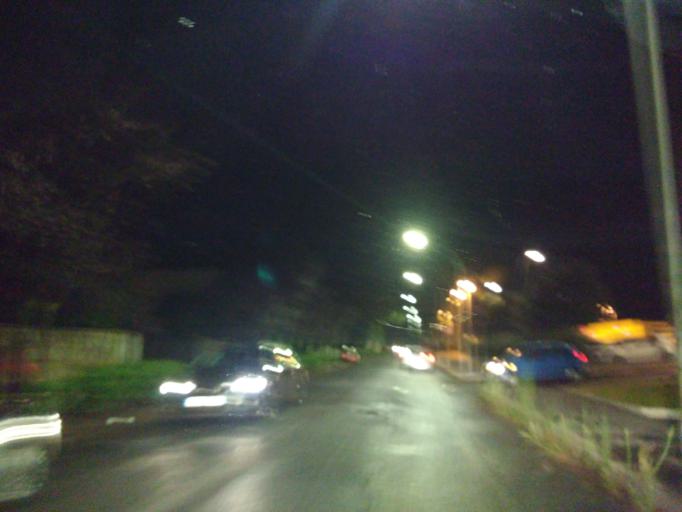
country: IT
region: Latium
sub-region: Citta metropolitana di Roma Capitale
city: Acilia-Castel Fusano-Ostia Antica
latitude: 41.7573
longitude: 12.3665
